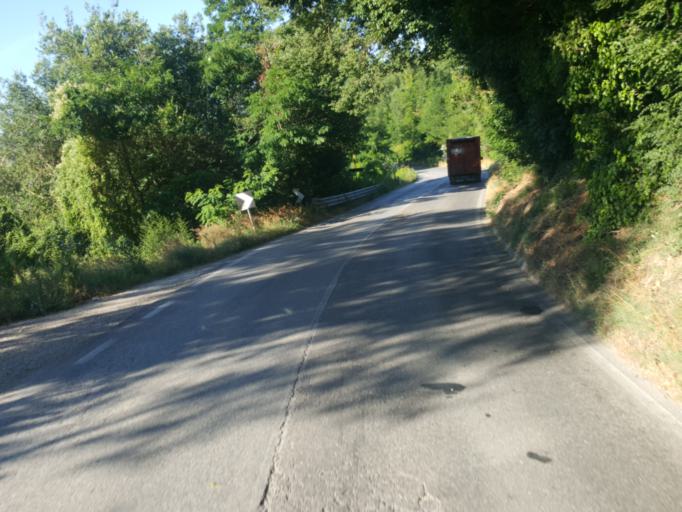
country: IT
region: The Marches
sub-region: Provincia di Pesaro e Urbino
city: Borgo Massano
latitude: 43.8126
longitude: 12.6634
